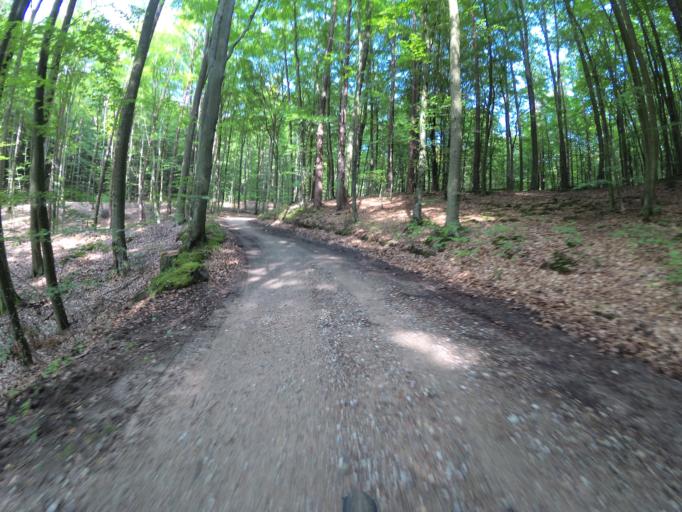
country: PL
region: Pomeranian Voivodeship
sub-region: Gdynia
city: Wielki Kack
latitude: 54.4941
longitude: 18.4774
